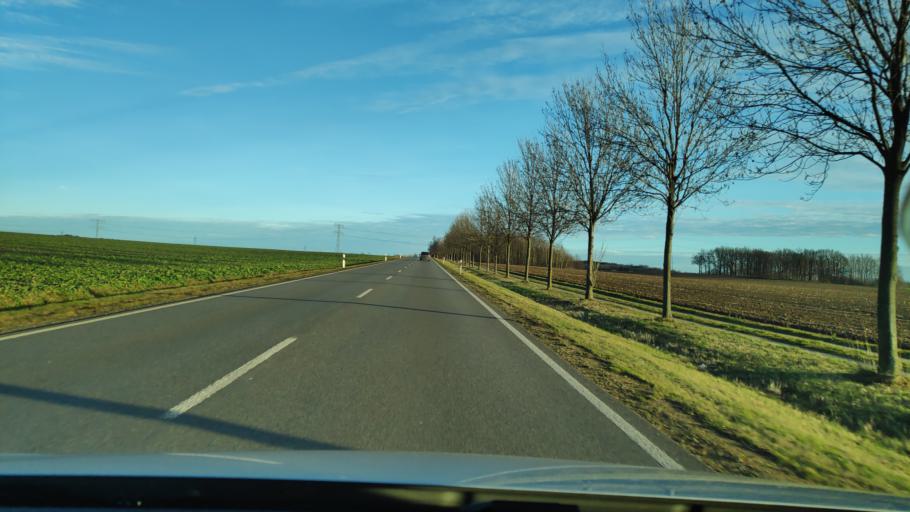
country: DE
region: Saxony
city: Zwickau
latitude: 50.7661
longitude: 12.5099
